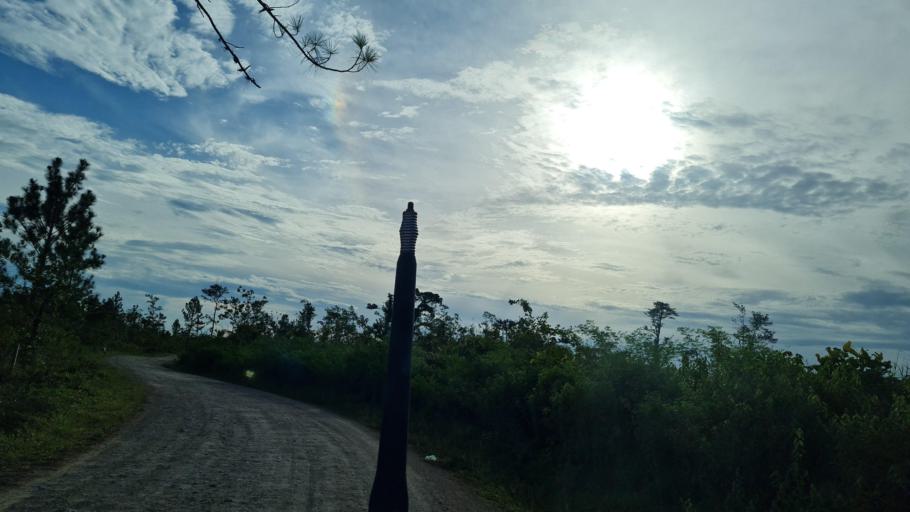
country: NI
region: Atlantico Sur
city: La Cruz de Rio Grande
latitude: 13.5561
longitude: -84.2902
